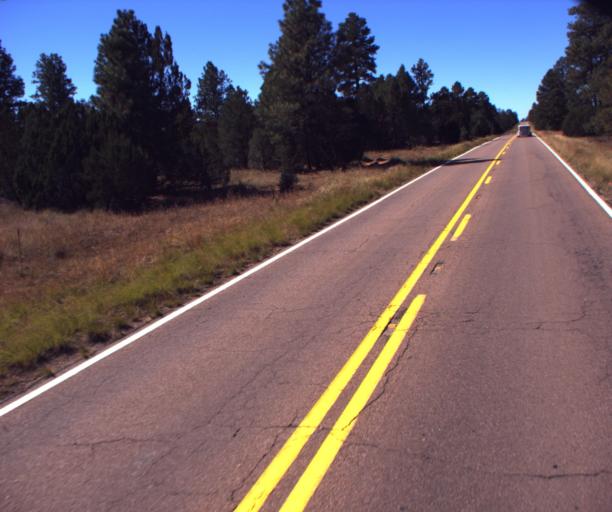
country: US
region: Arizona
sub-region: Navajo County
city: Heber-Overgaard
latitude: 34.4287
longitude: -110.5520
